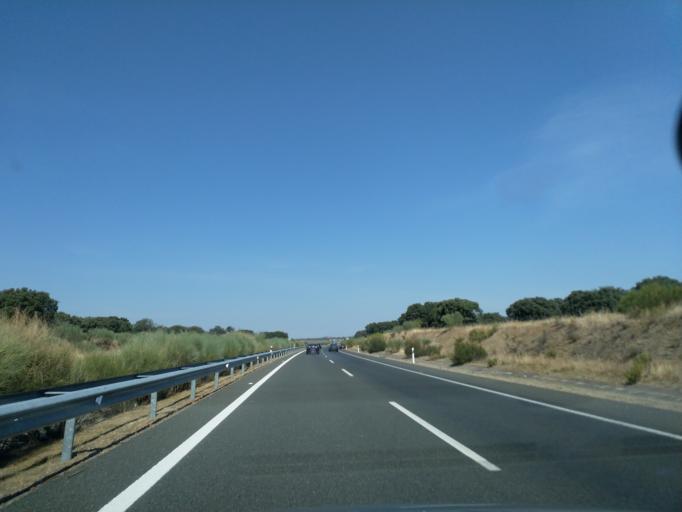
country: ES
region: Extremadura
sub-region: Provincia de Caceres
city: Aldea del Cano
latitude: 39.2697
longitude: -6.3210
